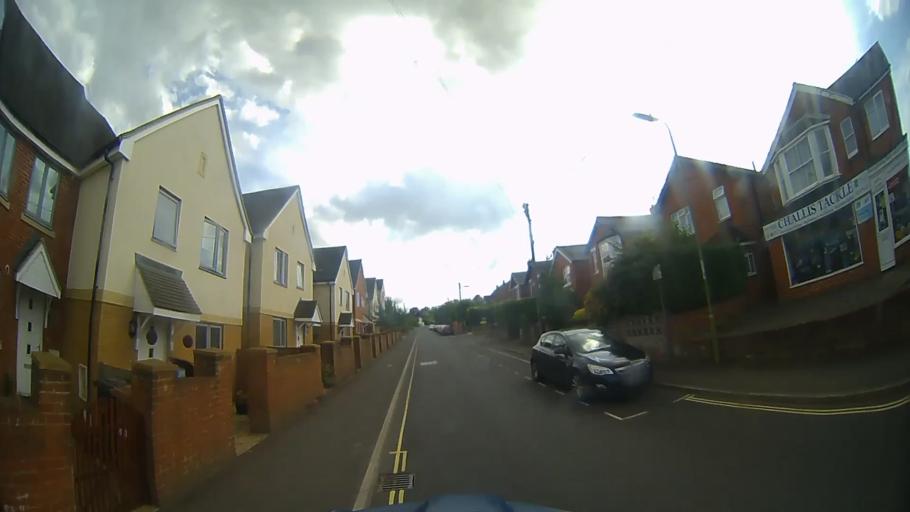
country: GB
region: England
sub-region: Hampshire
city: Andover
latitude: 51.2103
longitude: -1.4963
